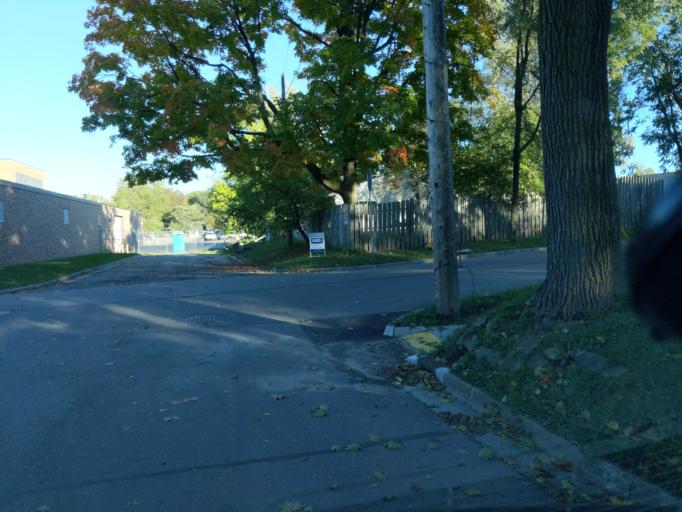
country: US
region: Michigan
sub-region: Ingham County
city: Lansing
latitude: 42.7504
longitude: -84.5611
